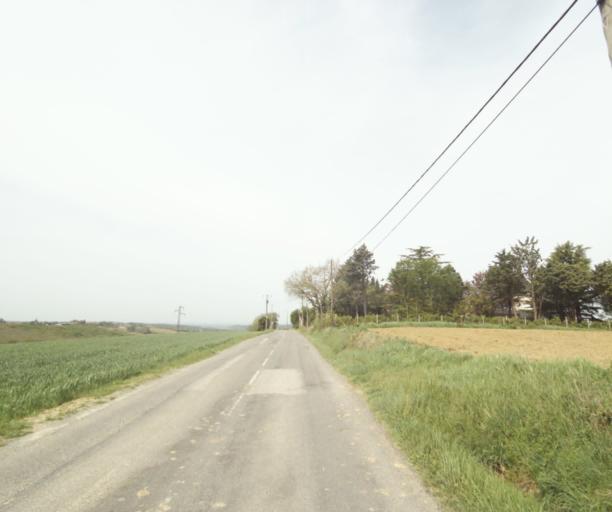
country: FR
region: Midi-Pyrenees
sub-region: Departement de la Haute-Garonne
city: Pechabou
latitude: 43.4906
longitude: 1.4966
